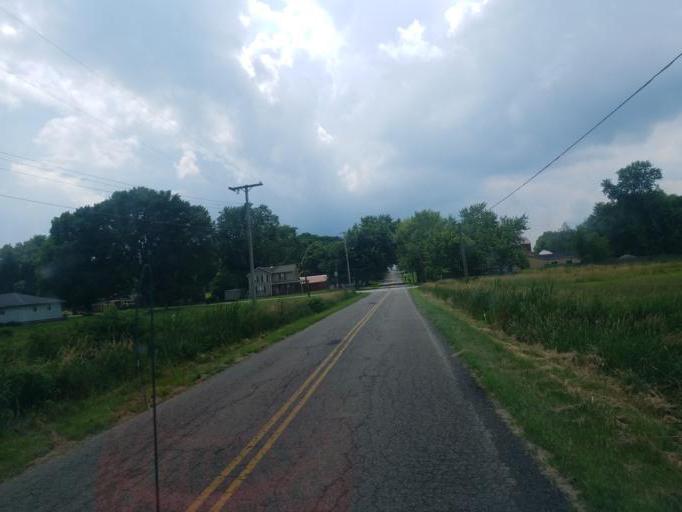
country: US
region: Ohio
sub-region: Columbiana County
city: Salem
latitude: 40.9740
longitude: -80.9045
